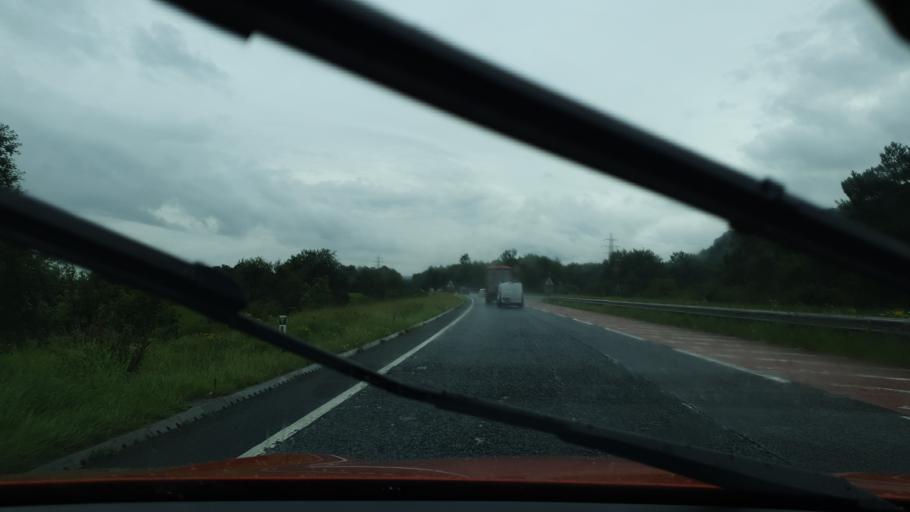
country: GB
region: England
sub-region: Cumbria
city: Arnside
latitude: 54.2582
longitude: -2.8212
